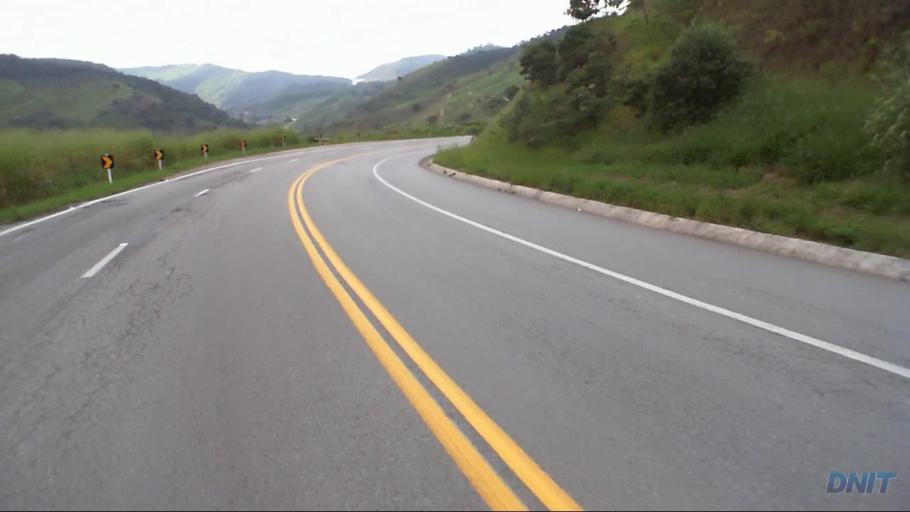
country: BR
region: Minas Gerais
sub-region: Nova Era
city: Nova Era
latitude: -19.6497
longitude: -42.9405
